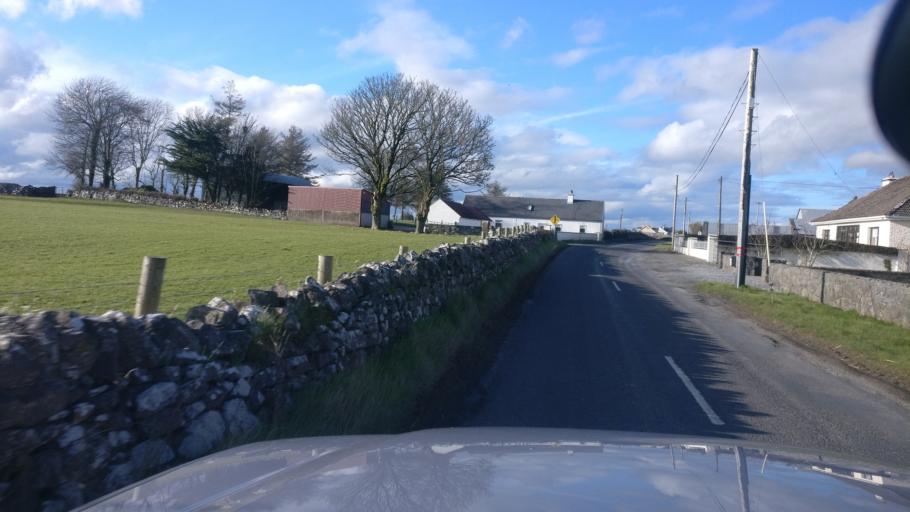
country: IE
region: Connaught
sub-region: County Galway
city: Loughrea
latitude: 53.2018
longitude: -8.4020
